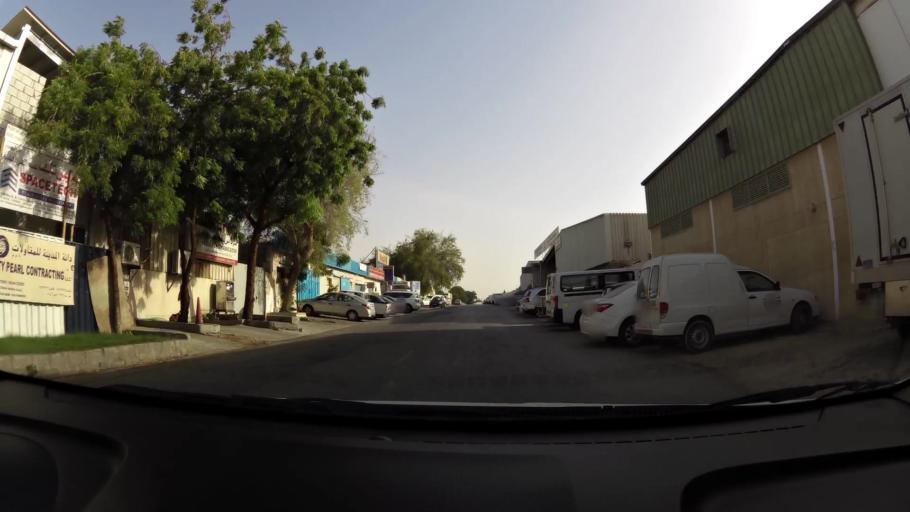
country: AE
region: Ash Shariqah
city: Sharjah
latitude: 25.2360
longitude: 55.3747
